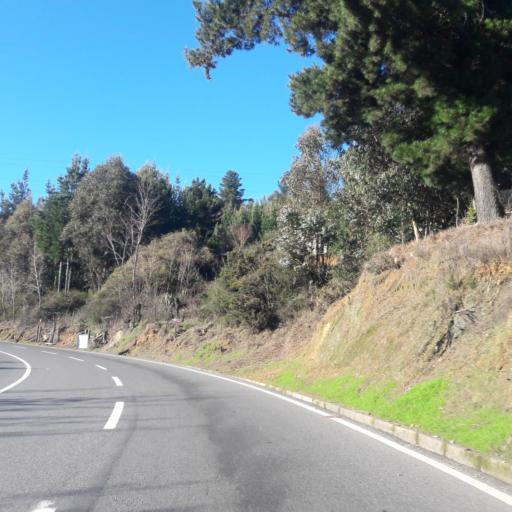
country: CL
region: Biobio
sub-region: Provincia de Biobio
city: La Laja
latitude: -37.2687
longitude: -72.9622
